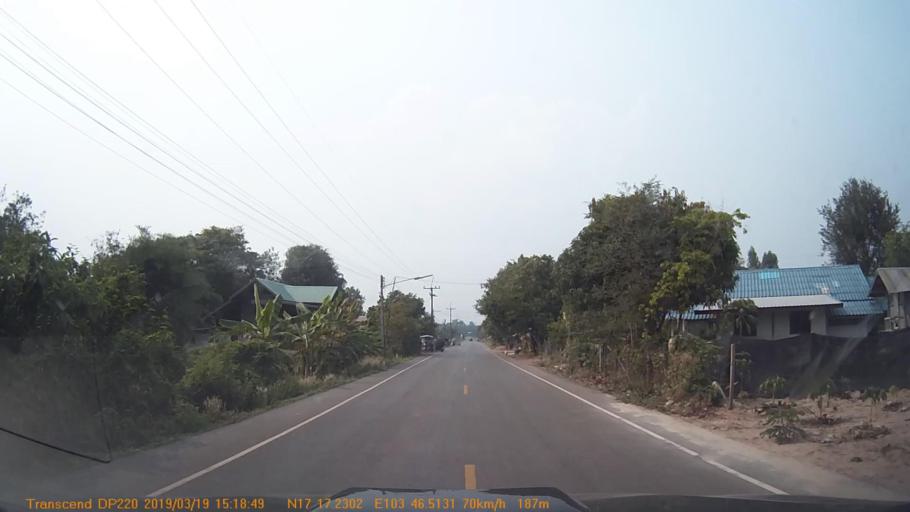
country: TH
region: Sakon Nakhon
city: Phanna Nikhom
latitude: 17.2874
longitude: 103.7751
